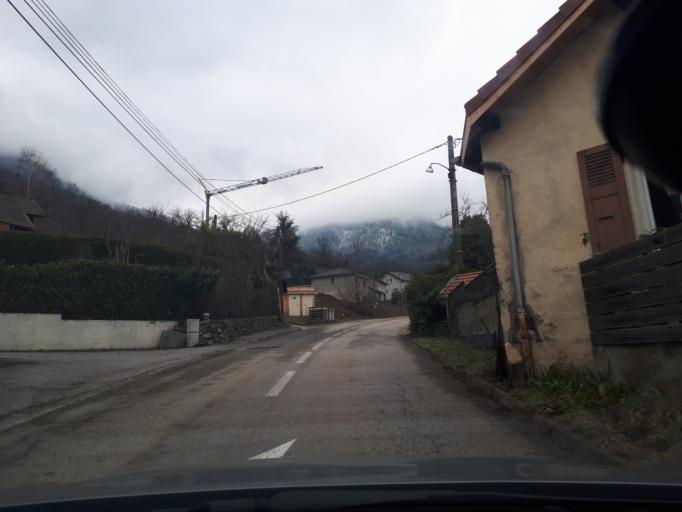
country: FR
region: Rhone-Alpes
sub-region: Departement de l'Isere
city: Vaulnaveys-le-Haut
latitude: 45.1189
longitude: 5.8287
